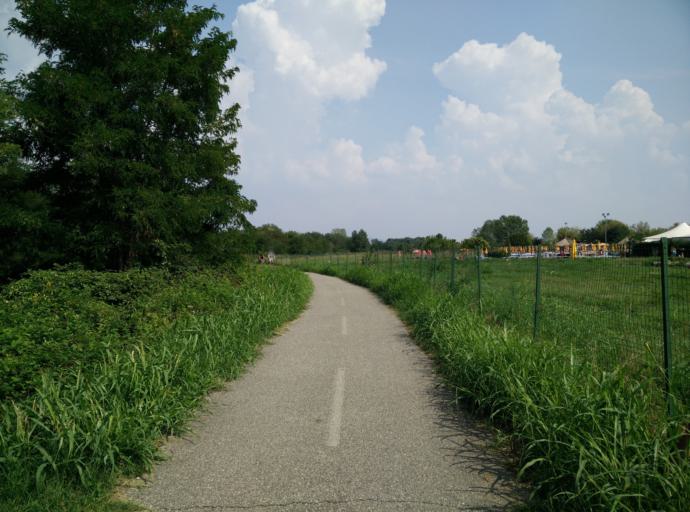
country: IT
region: Piedmont
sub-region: Provincia di Torino
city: Orbassano
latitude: 45.0162
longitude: 7.5400
